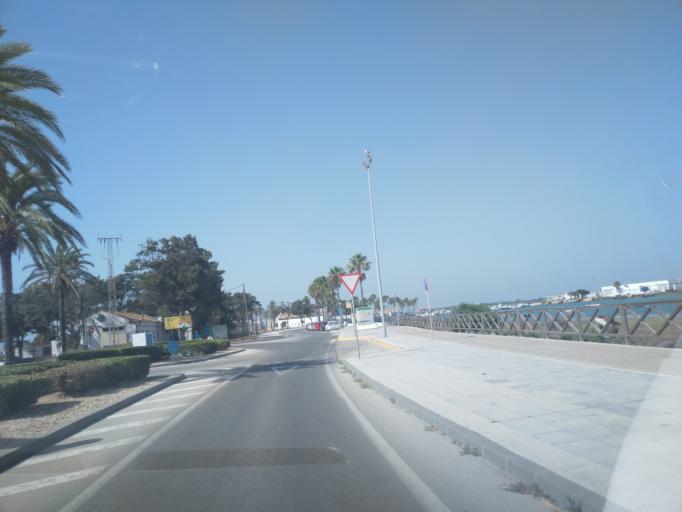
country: ES
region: Andalusia
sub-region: Provincia de Cadiz
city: Chiclana de la Frontera
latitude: 36.3924
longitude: -6.2074
